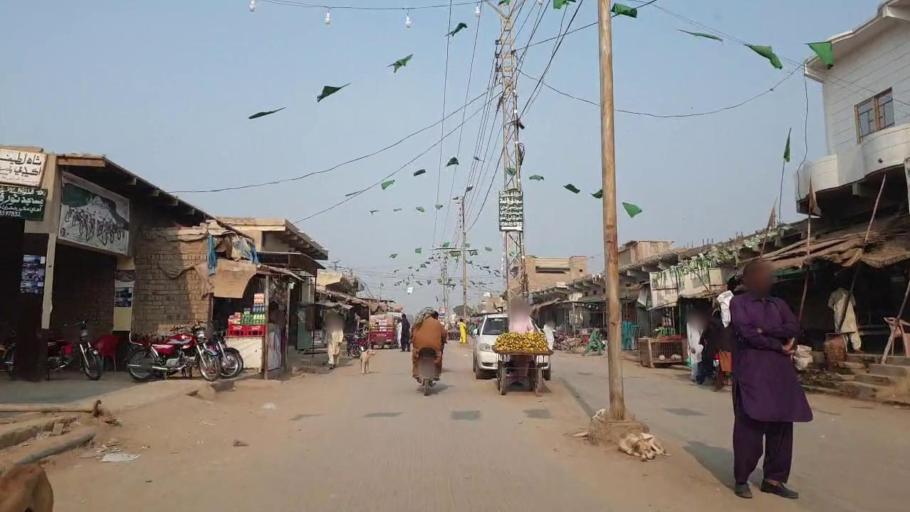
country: PK
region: Sindh
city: Bhan
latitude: 26.5617
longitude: 67.7224
